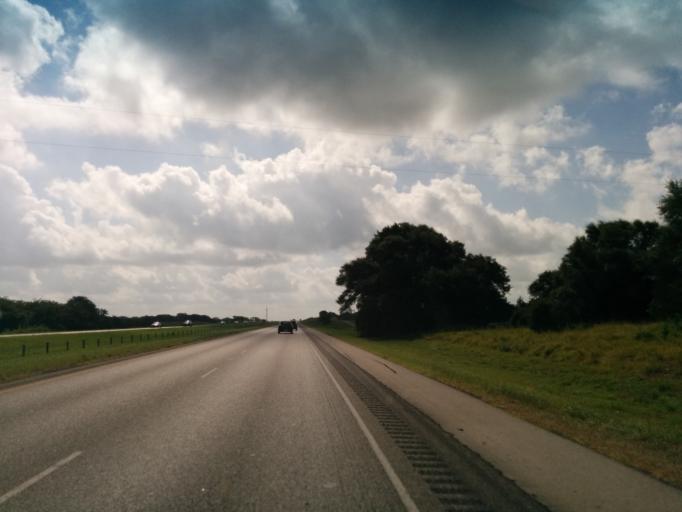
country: US
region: Texas
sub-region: Fayette County
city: Flatonia
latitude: 29.6959
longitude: -97.0338
